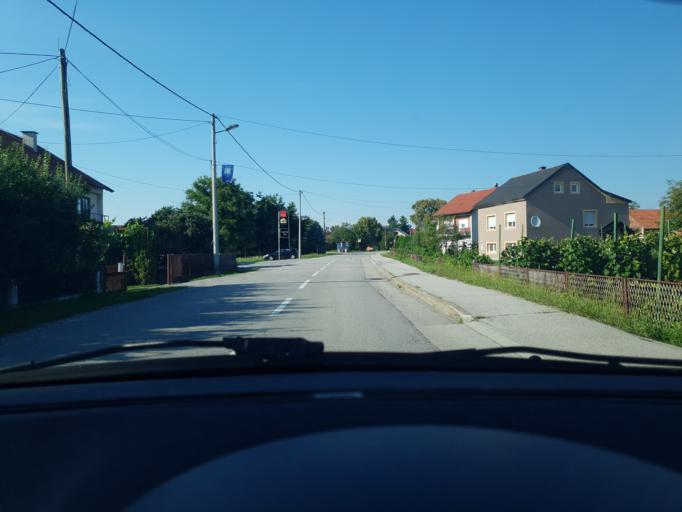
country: HR
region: Zagrebacka
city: Jakovlje
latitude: 45.9440
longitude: 15.8457
